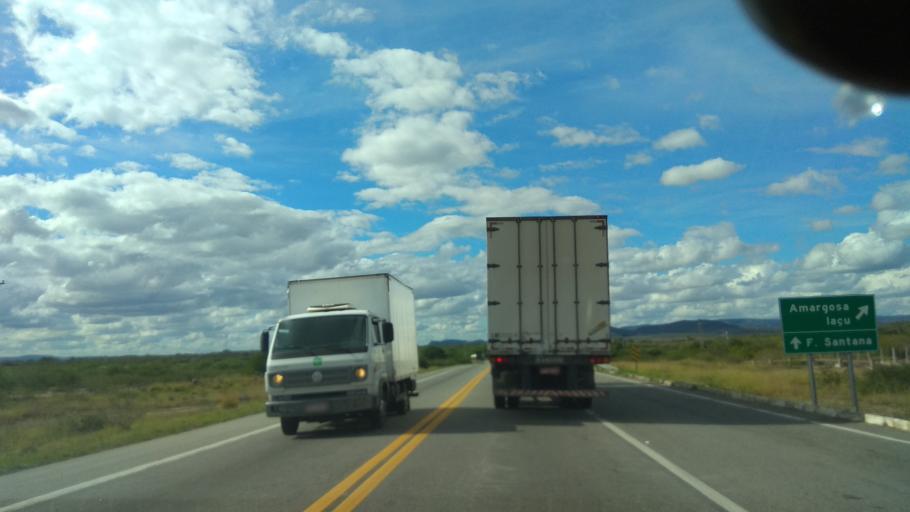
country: BR
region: Bahia
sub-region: Amargosa
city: Amargosa
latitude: -12.8492
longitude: -39.8429
